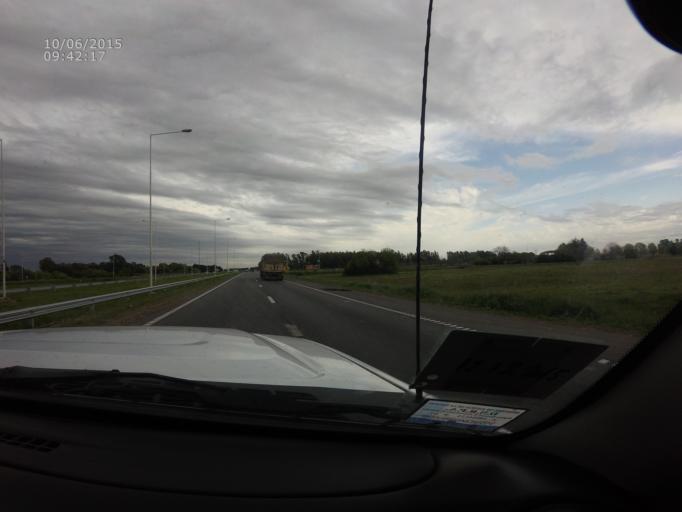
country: AR
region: Buenos Aires
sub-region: Partido de Zarate
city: Zarate
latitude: -34.0726
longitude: -59.2319
